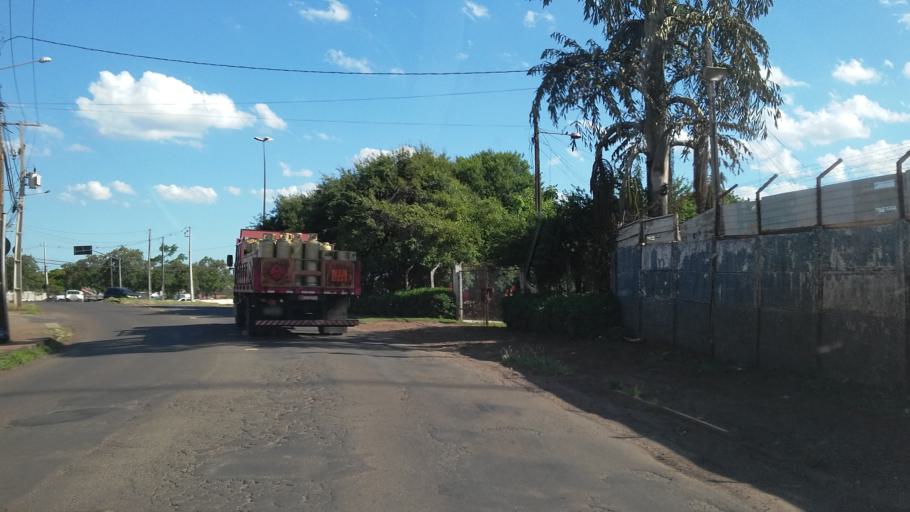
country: BR
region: Parana
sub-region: Londrina
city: Londrina
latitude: -23.2941
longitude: -51.2090
